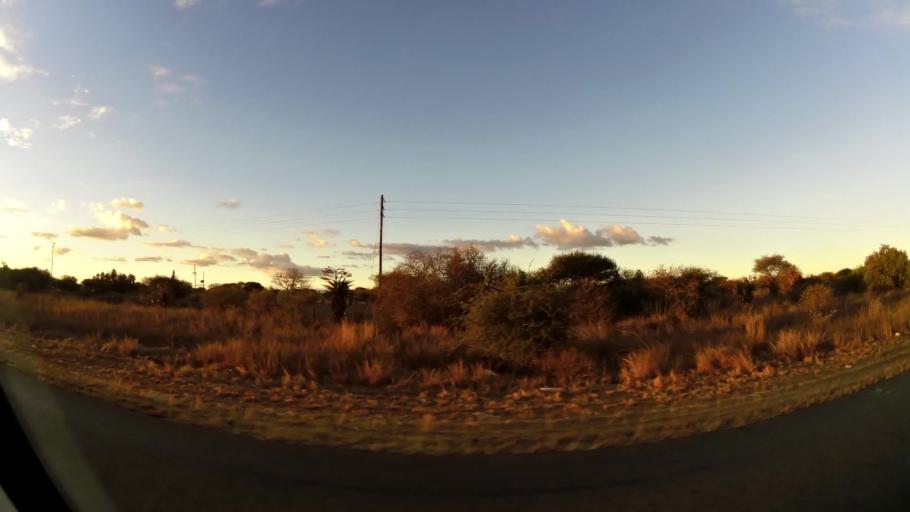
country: ZA
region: Limpopo
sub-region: Capricorn District Municipality
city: Polokwane
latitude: -23.8300
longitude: 29.4855
